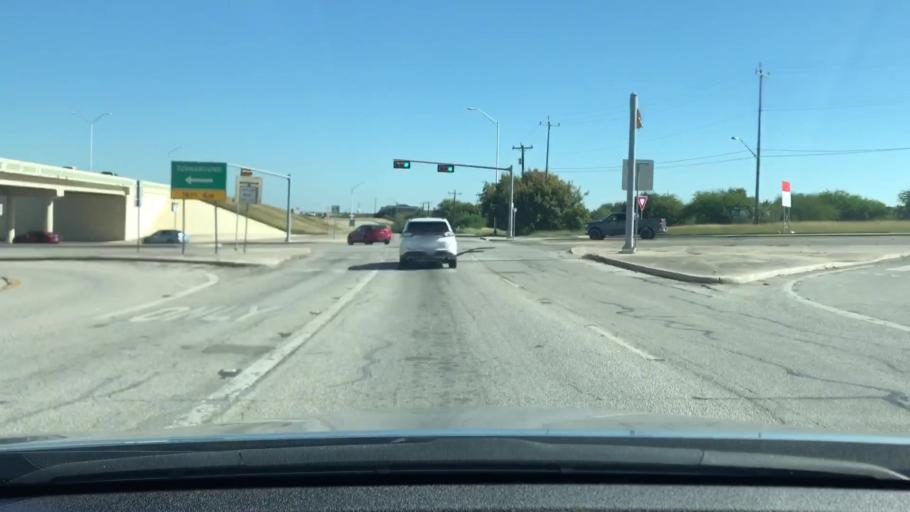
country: US
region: Texas
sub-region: Bexar County
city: Universal City
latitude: 29.5466
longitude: -98.3164
